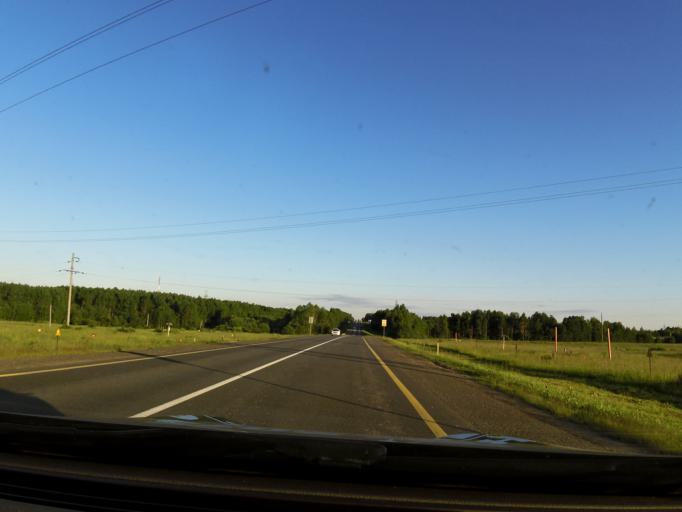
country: RU
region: Vologda
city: Gryazovets
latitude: 58.7924
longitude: 40.2676
